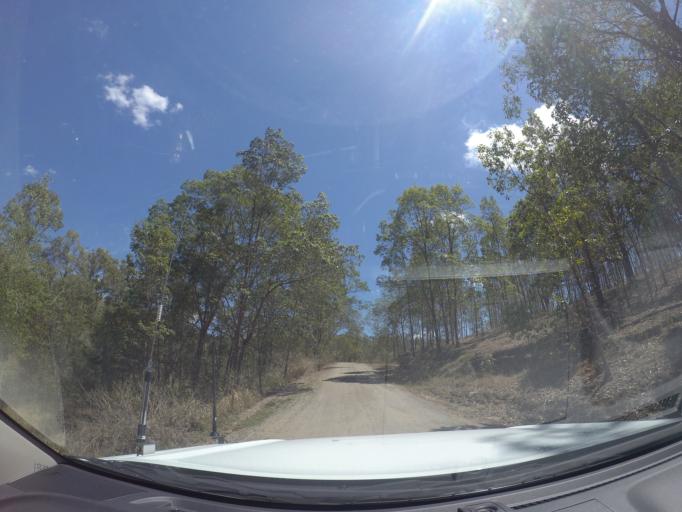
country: AU
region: Queensland
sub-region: Ipswich
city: Springfield Lakes
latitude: -27.8177
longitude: 152.8488
